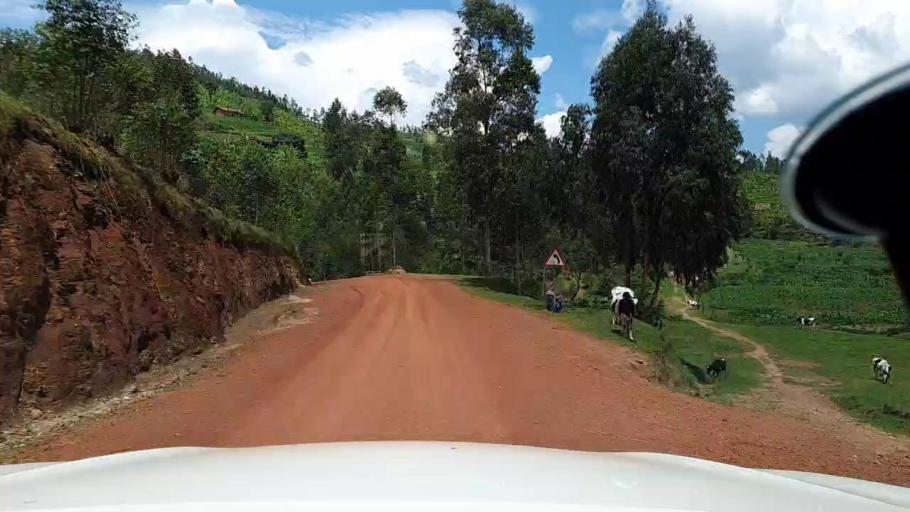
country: RW
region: Northern Province
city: Byumba
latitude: -1.7047
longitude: 29.8477
